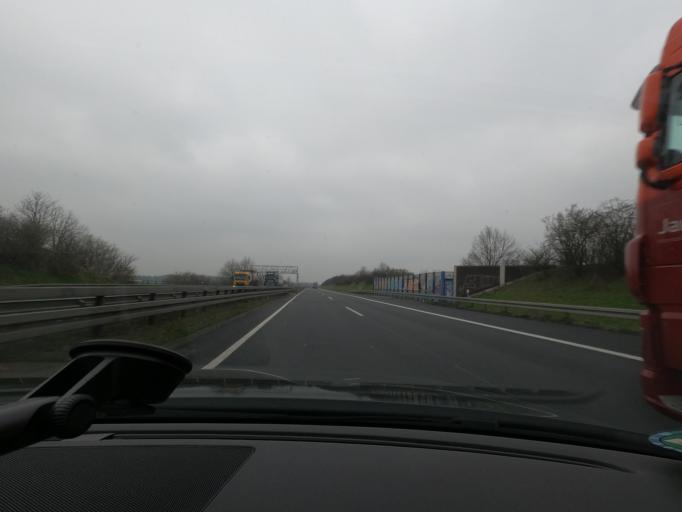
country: DE
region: North Rhine-Westphalia
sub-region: Regierungsbezirk Dusseldorf
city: Nettetal
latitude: 51.3036
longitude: 6.2407
